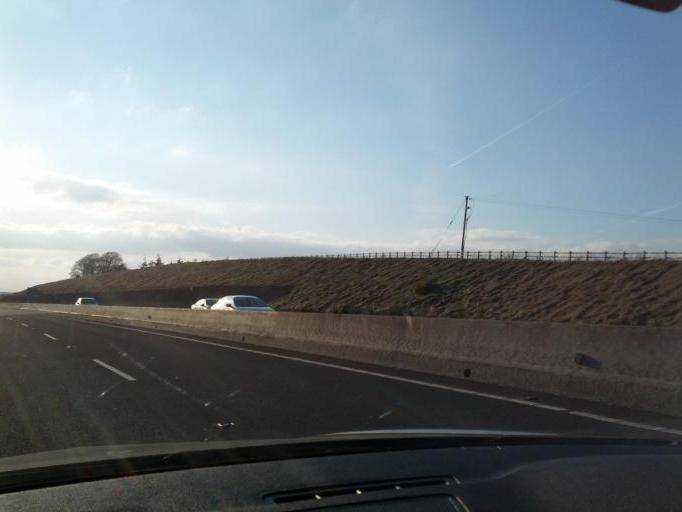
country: IE
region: Munster
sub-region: North Tipperary
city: Templemore
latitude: 52.8875
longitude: -7.9332
